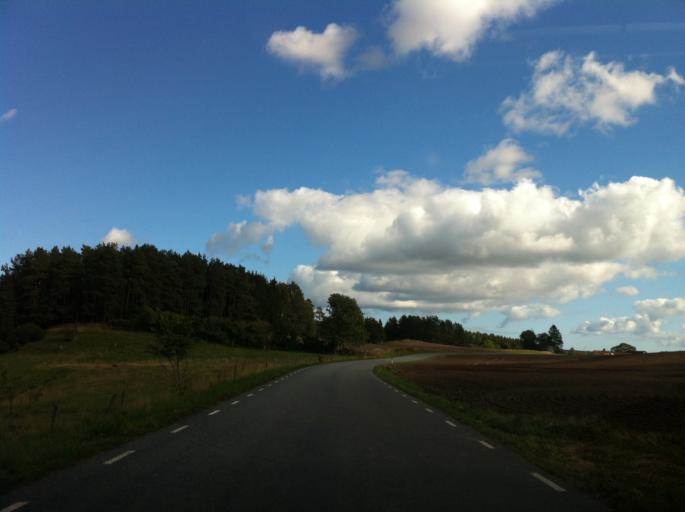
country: SE
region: Skane
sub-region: Kristianstads Kommun
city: Degeberga
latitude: 55.7060
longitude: 14.0005
